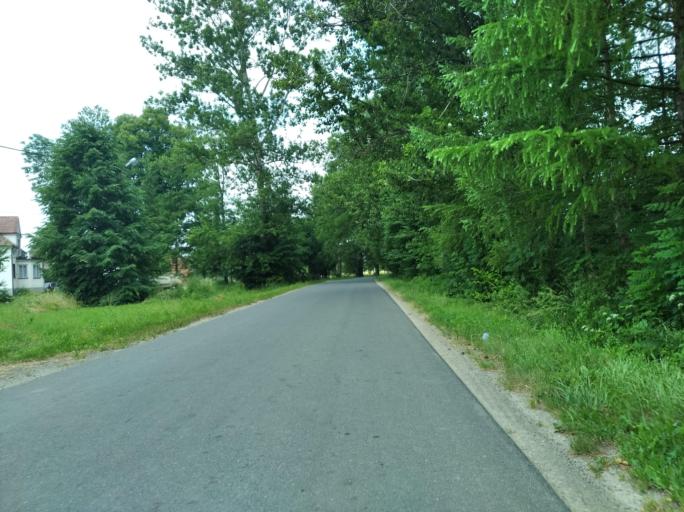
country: PL
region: Subcarpathian Voivodeship
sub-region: Powiat sanocki
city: Besko
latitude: 49.6238
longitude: 21.9355
